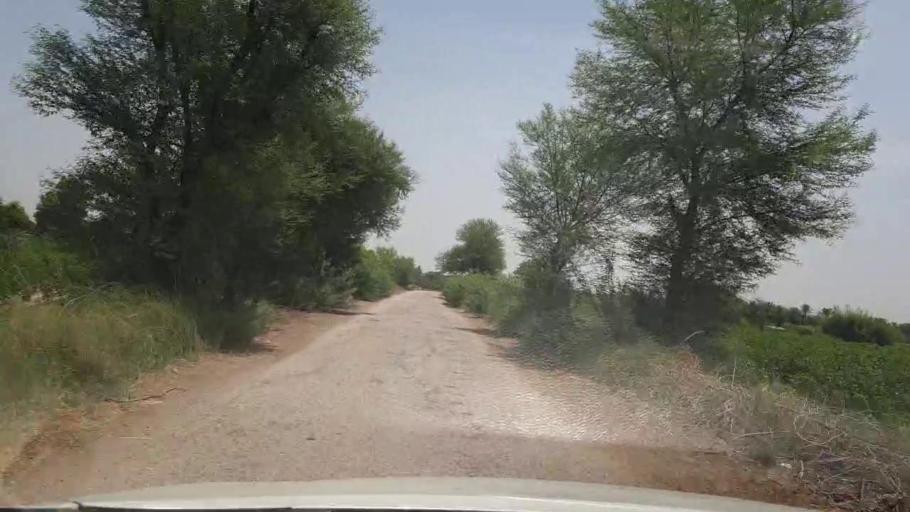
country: PK
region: Sindh
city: Bozdar
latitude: 27.2046
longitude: 68.6716
